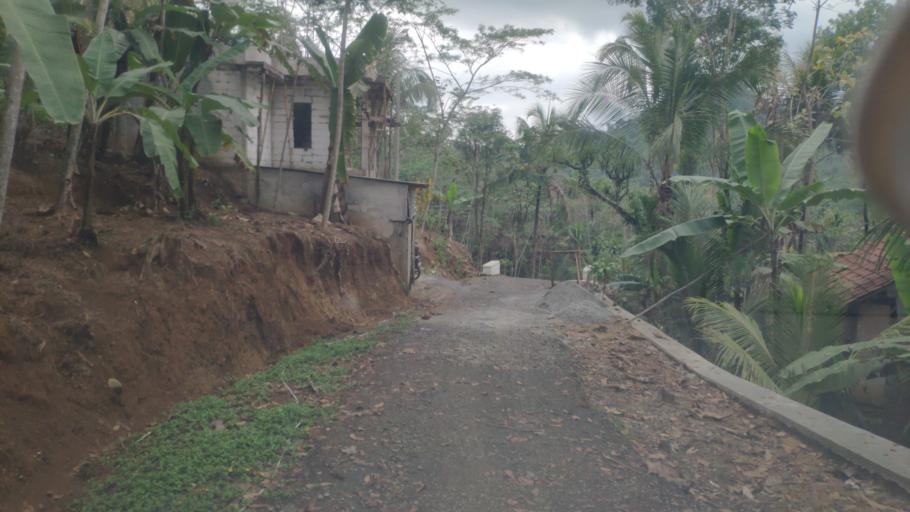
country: ID
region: Central Java
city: Purbalingga
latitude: -7.3042
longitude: 109.5695
